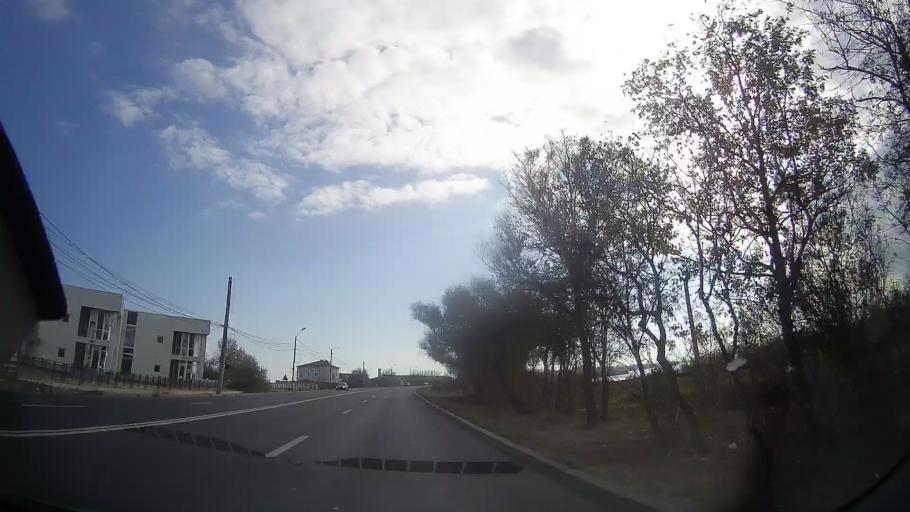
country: RO
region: Constanta
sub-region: Oras Eforie
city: Eforie Nord
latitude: 44.0558
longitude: 28.6399
